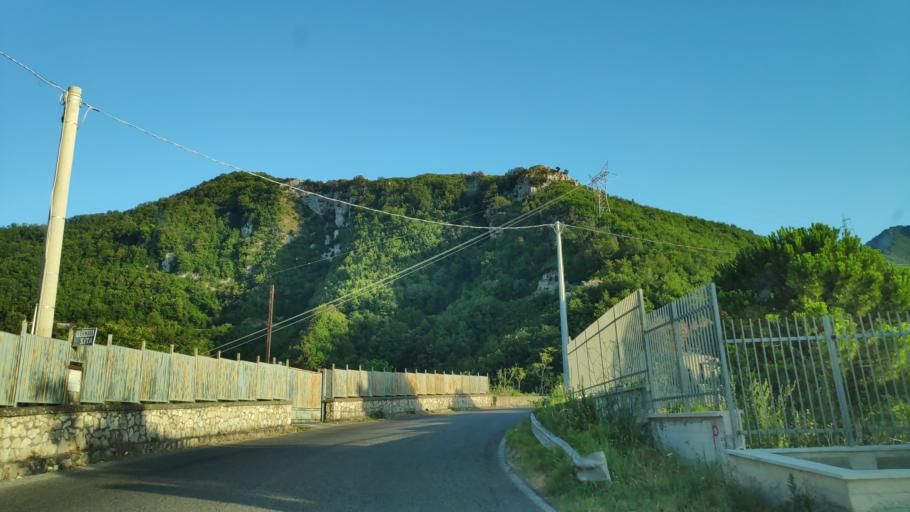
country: IT
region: Campania
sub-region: Provincia di Salerno
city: Corbara
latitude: 40.7225
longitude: 14.6053
